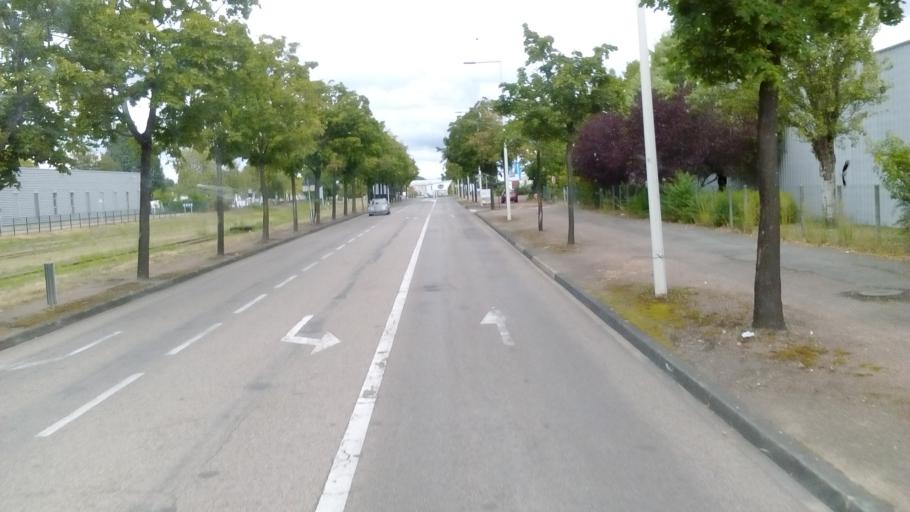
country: FR
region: Rhone-Alpes
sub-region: Departement de la Loire
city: Roanne
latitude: 46.0551
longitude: 4.0827
